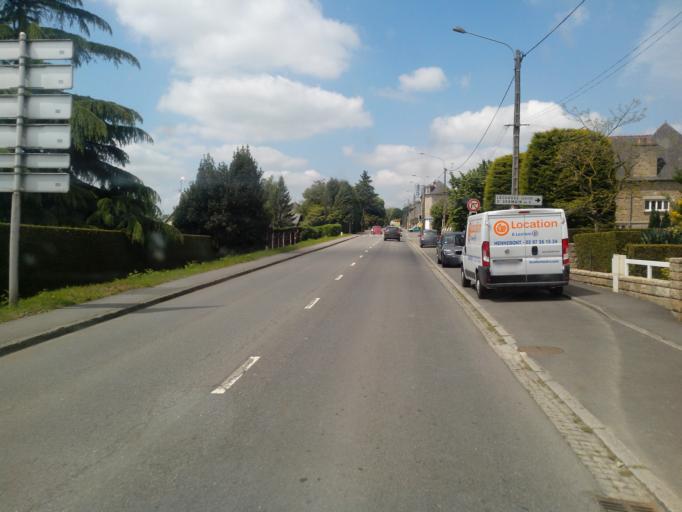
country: FR
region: Brittany
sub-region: Departement d'Ille-et-Vilaine
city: Lecousse
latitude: 48.3627
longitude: -1.2124
